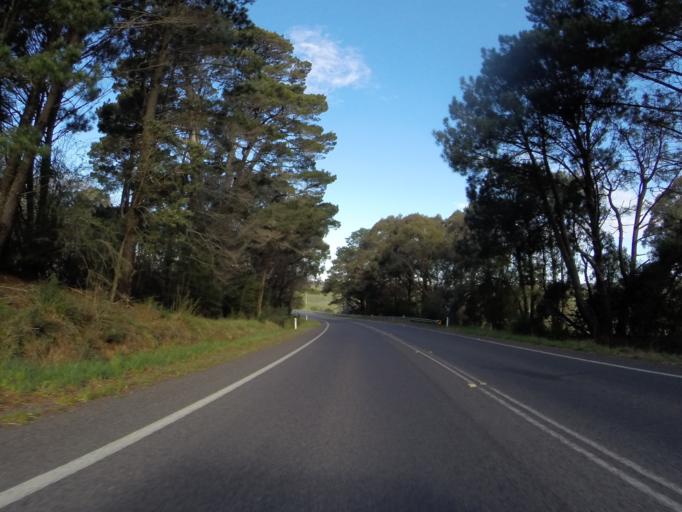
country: AU
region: New South Wales
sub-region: Wingecarribee
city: Moss Vale
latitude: -34.5639
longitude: 150.4045
